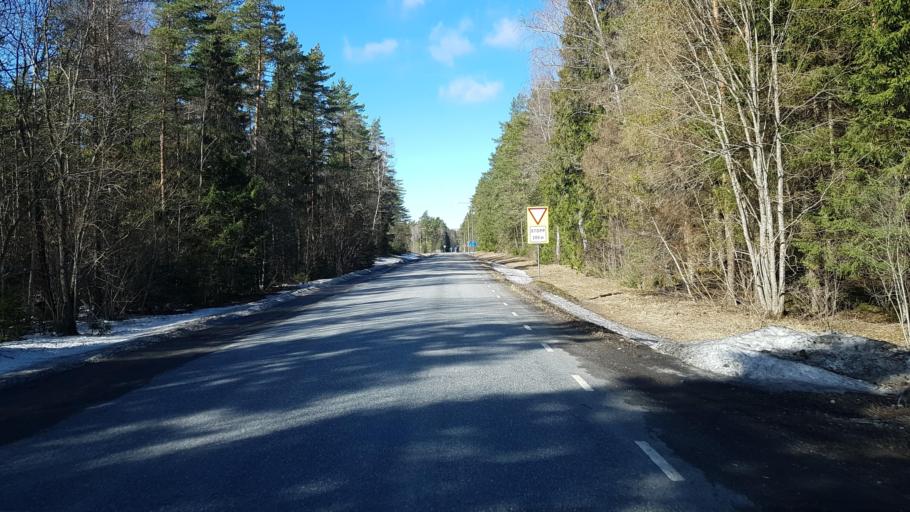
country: EE
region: Raplamaa
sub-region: Maerjamaa vald
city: Marjamaa
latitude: 58.8962
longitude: 24.4606
